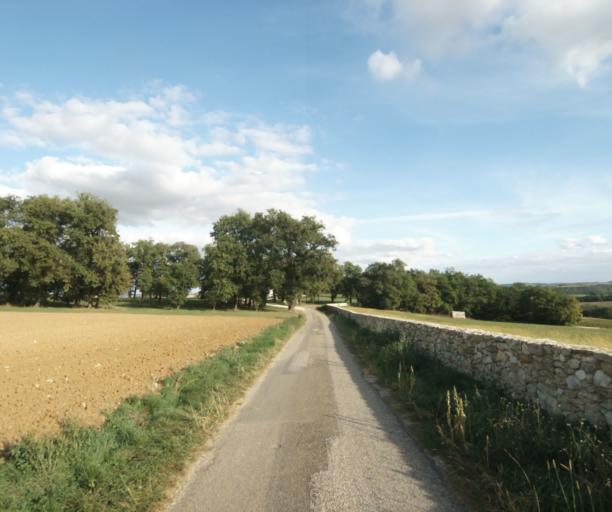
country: FR
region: Midi-Pyrenees
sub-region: Departement du Gers
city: Gondrin
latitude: 43.8949
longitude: 0.2691
